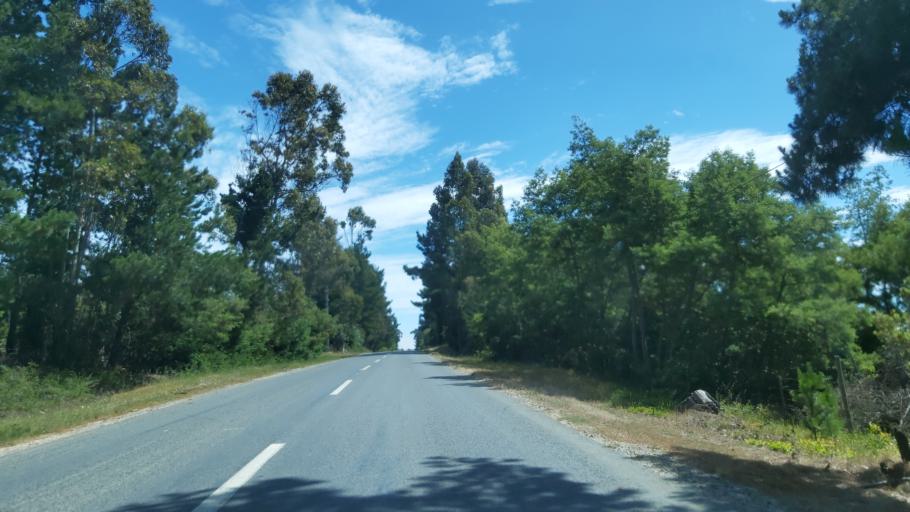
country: CL
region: Maule
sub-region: Provincia de Talca
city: Constitucion
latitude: -35.5611
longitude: -72.5892
